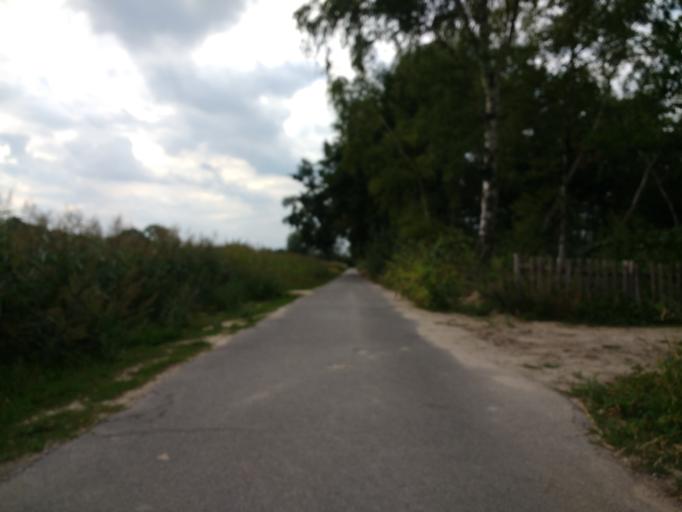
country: DE
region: Lower Saxony
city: Calberlah
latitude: 52.4262
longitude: 10.6554
